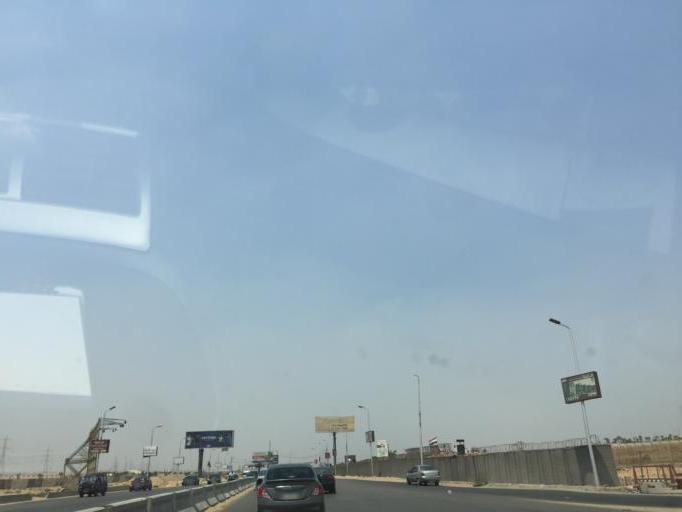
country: EG
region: Muhafazat al Qalyubiyah
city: Al Khankah
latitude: 30.0793
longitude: 31.4313
